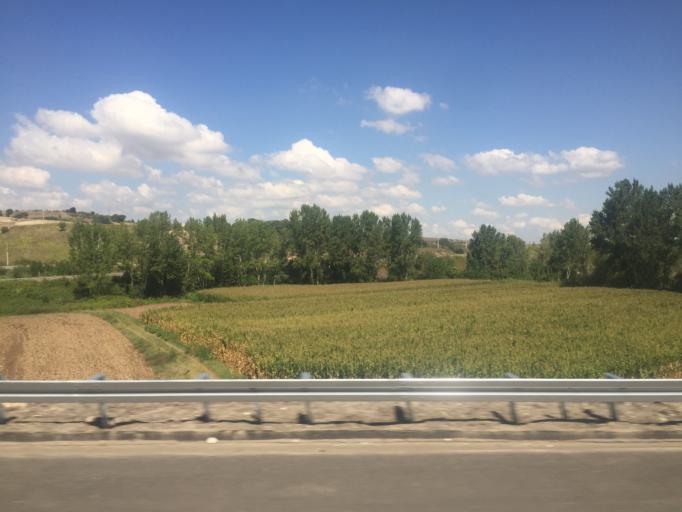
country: TR
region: Balikesir
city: Gobel
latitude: 39.9801
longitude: 28.1756
